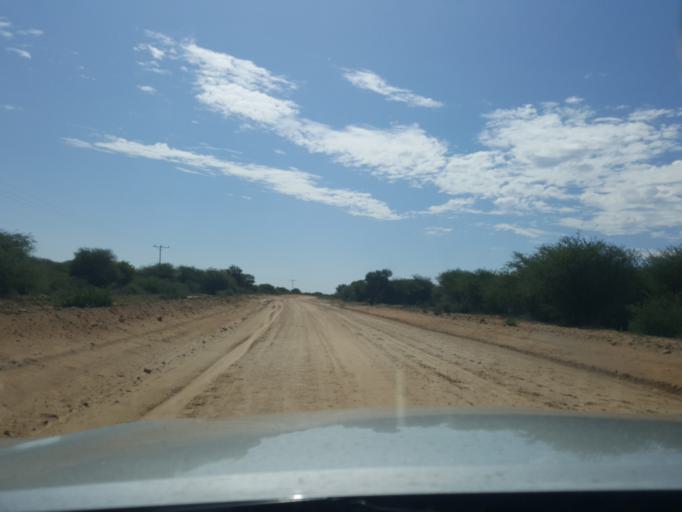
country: BW
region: Kweneng
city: Khudumelapye
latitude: -23.8877
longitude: 24.9157
